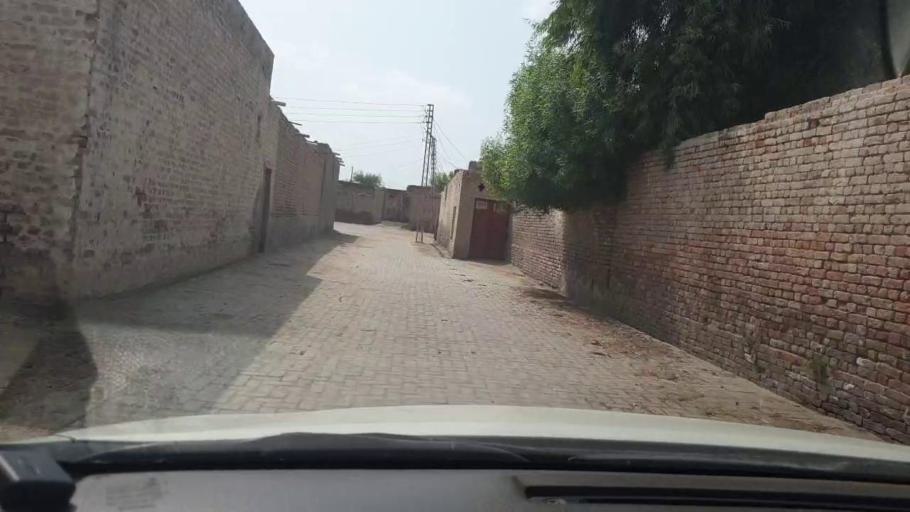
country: PK
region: Sindh
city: Shikarpur
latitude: 27.9932
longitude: 68.5835
